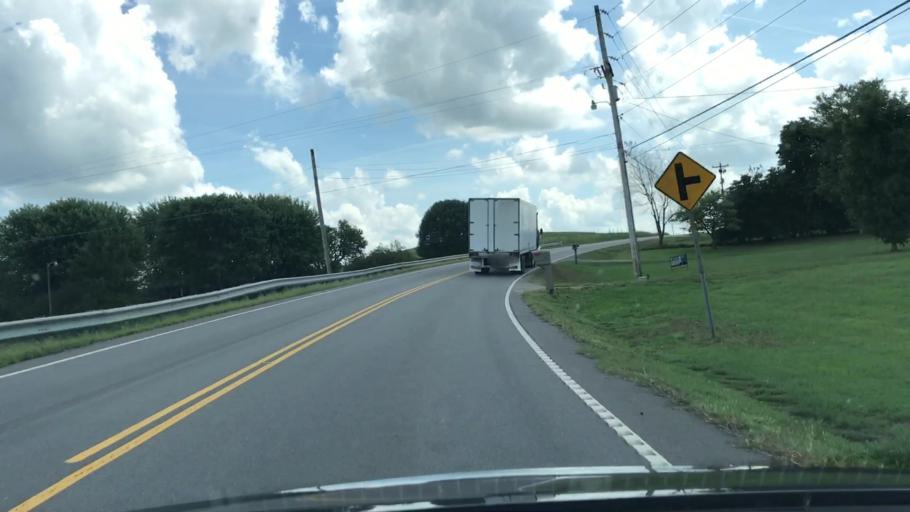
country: US
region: Tennessee
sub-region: Robertson County
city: Cross Plains
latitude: 36.5347
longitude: -86.6527
